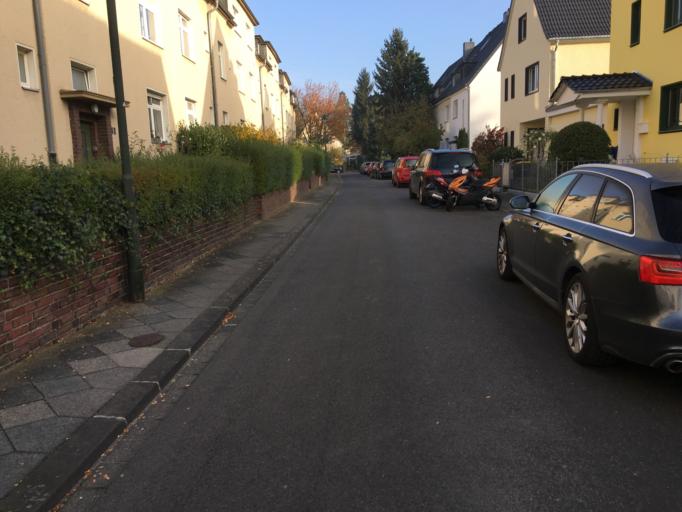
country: DE
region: North Rhine-Westphalia
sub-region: Regierungsbezirk Dusseldorf
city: Erkrath
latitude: 51.2399
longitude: 6.8549
